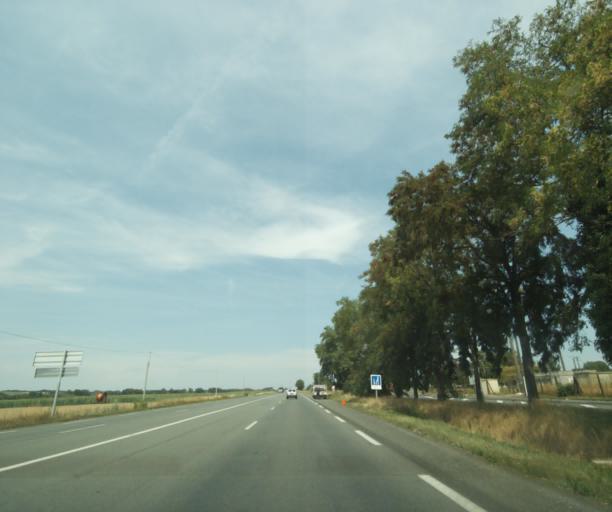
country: FR
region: Poitou-Charentes
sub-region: Departement de la Vienne
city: Dange-Saint-Romain
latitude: 46.9015
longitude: 0.5754
